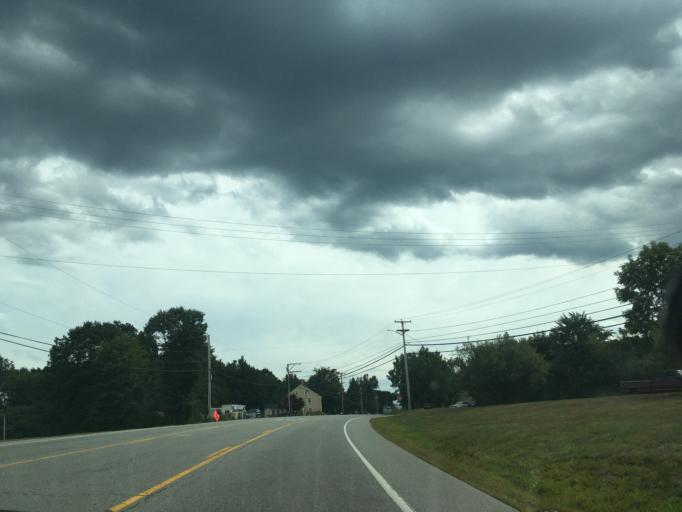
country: US
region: New Hampshire
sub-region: Rockingham County
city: Stratham Station
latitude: 43.0173
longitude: -70.9166
